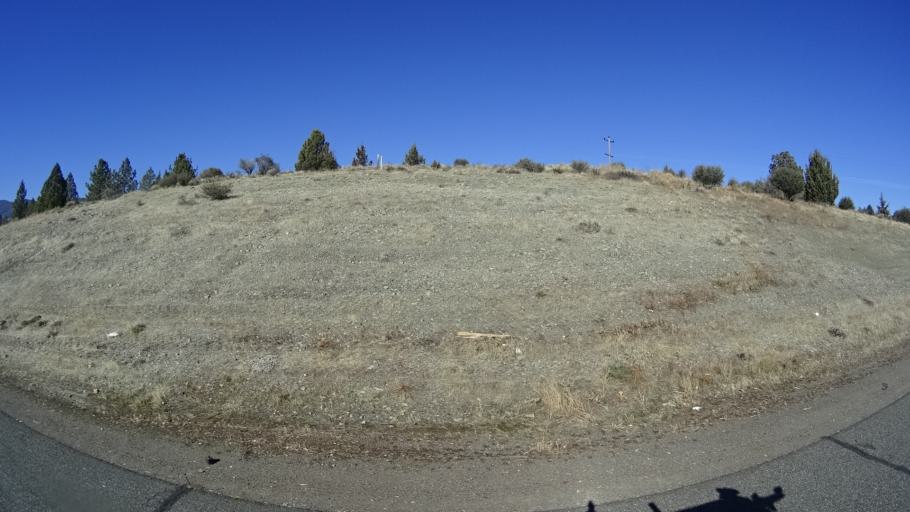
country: US
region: California
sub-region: Siskiyou County
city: Yreka
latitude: 41.7395
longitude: -122.6177
